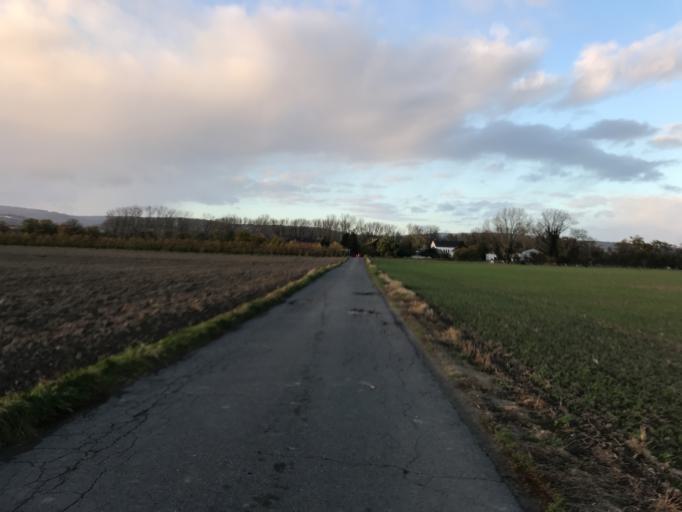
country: DE
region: Hesse
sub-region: Regierungsbezirk Darmstadt
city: Eltville
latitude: 50.0098
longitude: 8.1195
